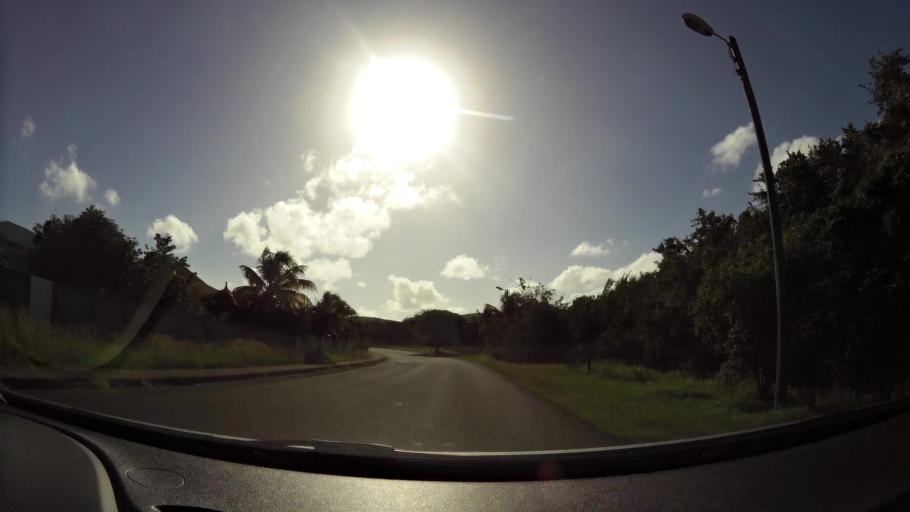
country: MQ
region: Martinique
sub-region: Martinique
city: Le Francois
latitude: 14.6204
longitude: -60.9022
